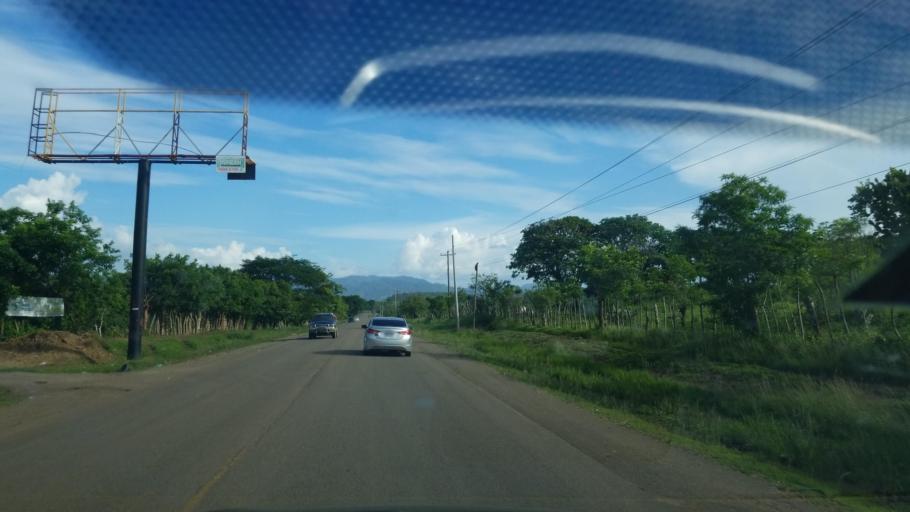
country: HN
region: El Paraiso
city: Arauli
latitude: 13.9388
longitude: -86.5586
